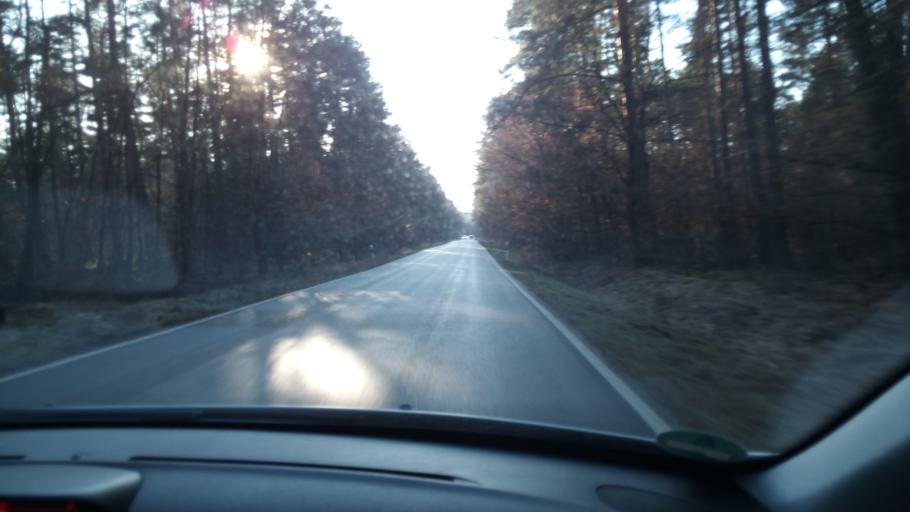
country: DE
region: Schleswig-Holstein
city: Brothen
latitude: 53.5052
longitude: 10.6845
